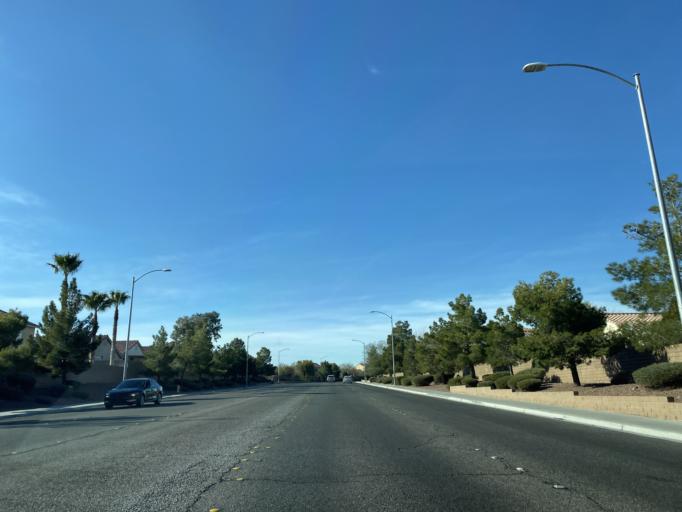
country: US
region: Nevada
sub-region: Clark County
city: Summerlin South
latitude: 36.3040
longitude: -115.2860
